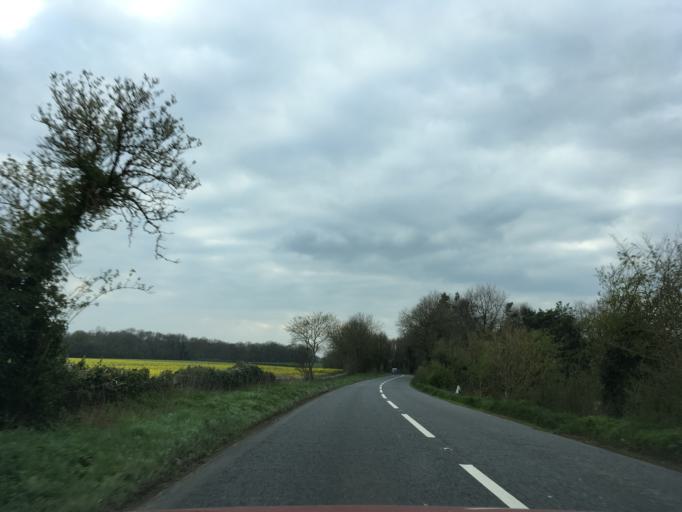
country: GB
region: England
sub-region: Gloucestershire
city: Coates
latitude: 51.6715
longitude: -2.0304
